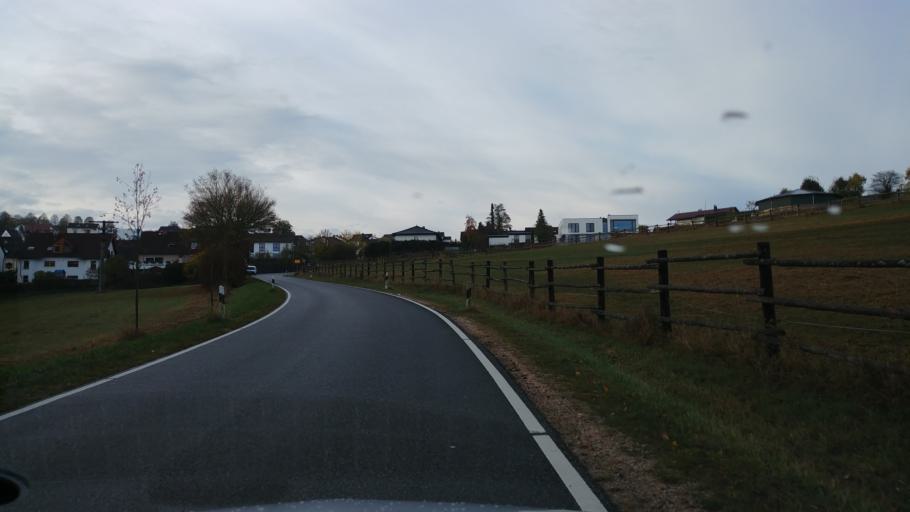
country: DE
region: Hesse
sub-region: Regierungsbezirk Darmstadt
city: Schlangenbad
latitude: 50.1289
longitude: 8.1192
